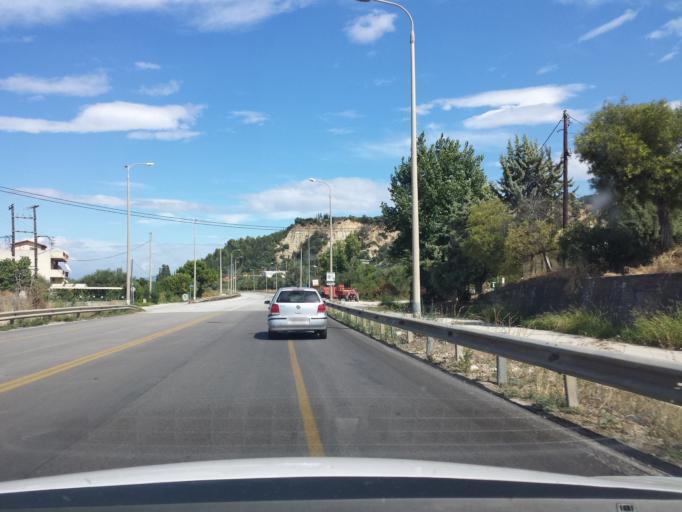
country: GR
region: West Greece
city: Vrachnaiika
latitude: 38.1463
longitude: 21.6204
